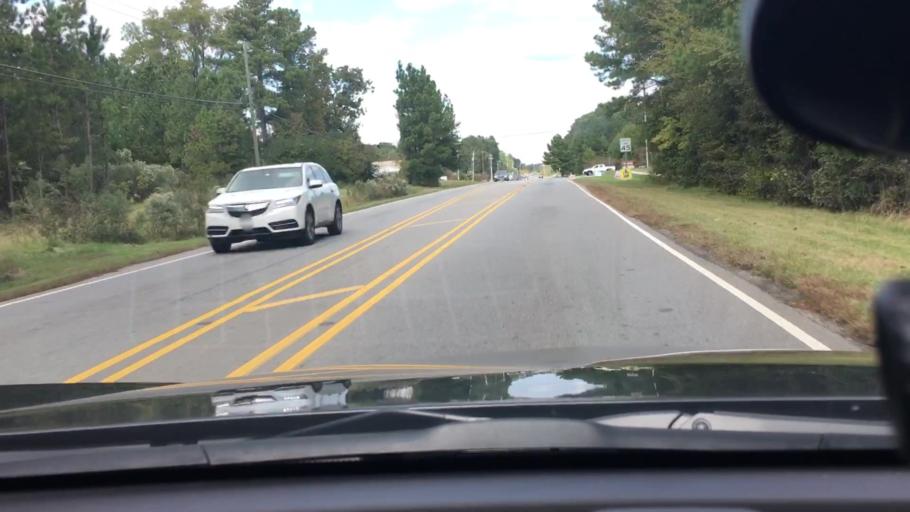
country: US
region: North Carolina
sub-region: Wake County
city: Holly Springs
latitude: 35.6869
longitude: -78.8340
